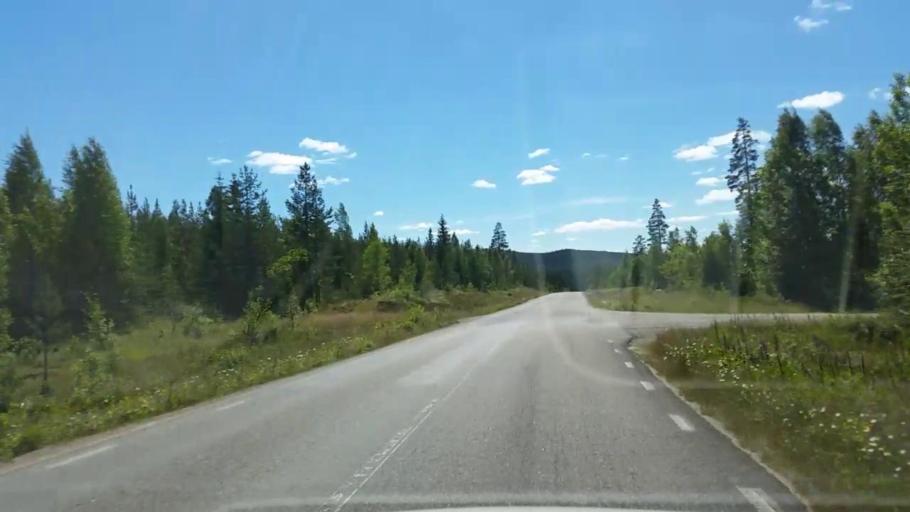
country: SE
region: Gaevleborg
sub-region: Ljusdals Kommun
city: Farila
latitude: 61.6446
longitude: 15.5927
